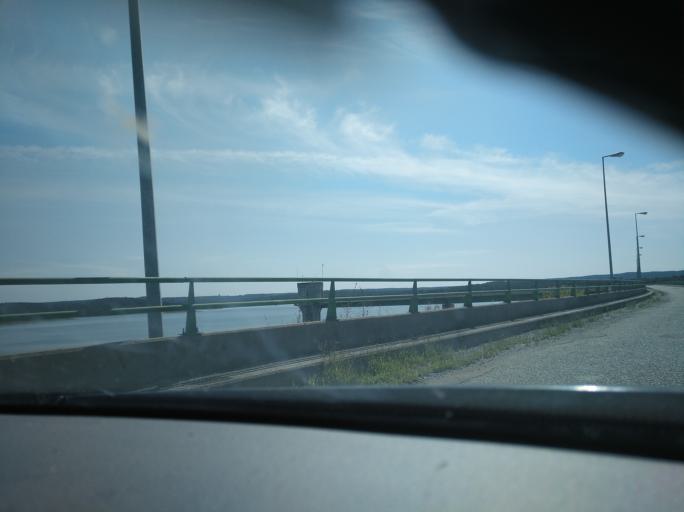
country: PT
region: Evora
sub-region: Montemor-O-Novo
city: Montemor-o-Novo
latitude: 38.6613
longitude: -8.0977
